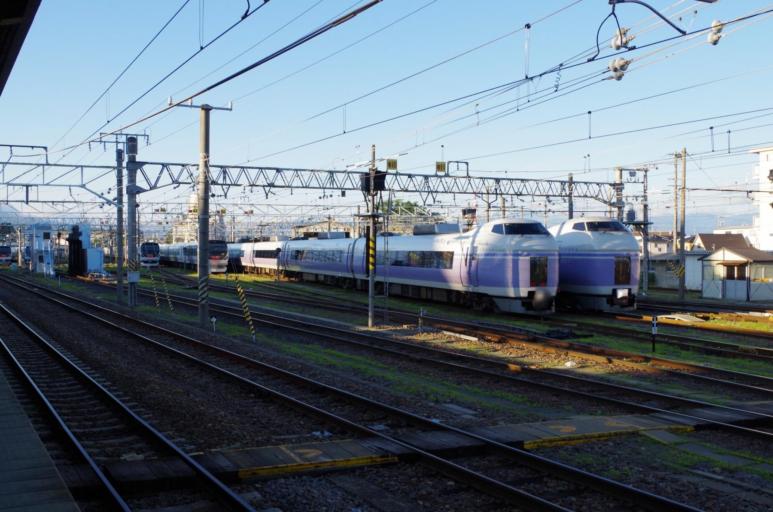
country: JP
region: Nagano
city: Matsumoto
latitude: 36.2302
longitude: 137.9645
